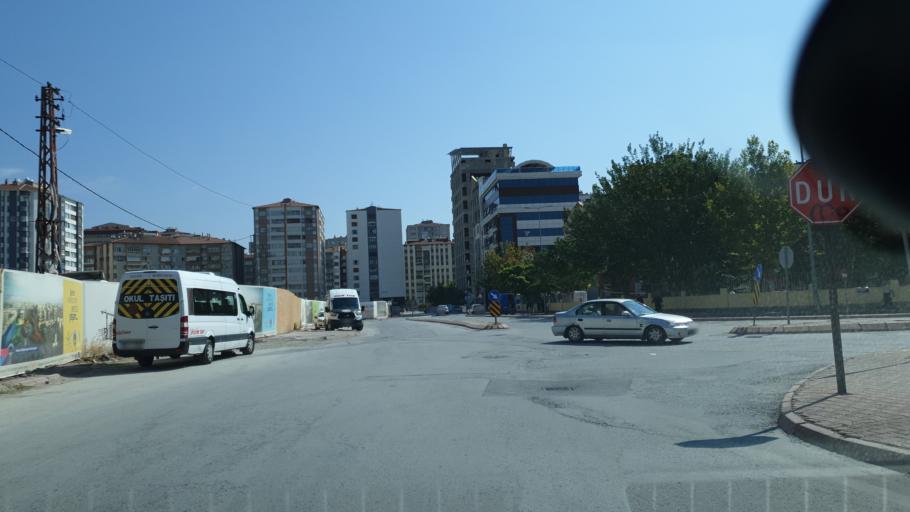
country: TR
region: Kayseri
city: Kayseri
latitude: 38.7267
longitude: 35.4909
